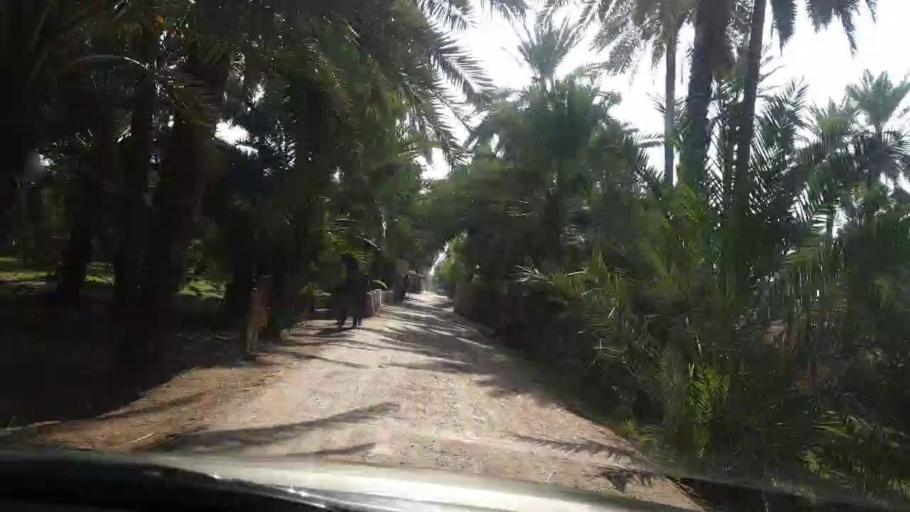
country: PK
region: Sindh
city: Sukkur
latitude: 27.6417
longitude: 68.8079
